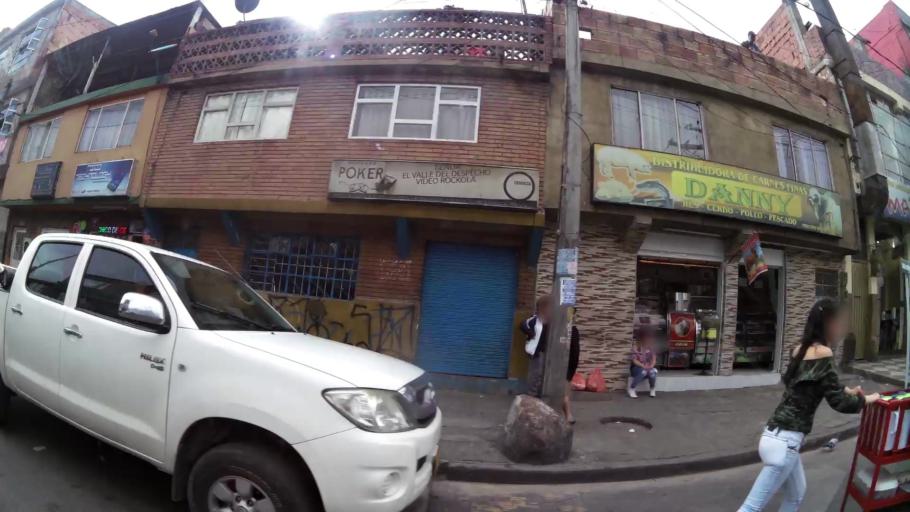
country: CO
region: Bogota D.C.
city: Bogota
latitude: 4.5563
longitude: -74.1120
